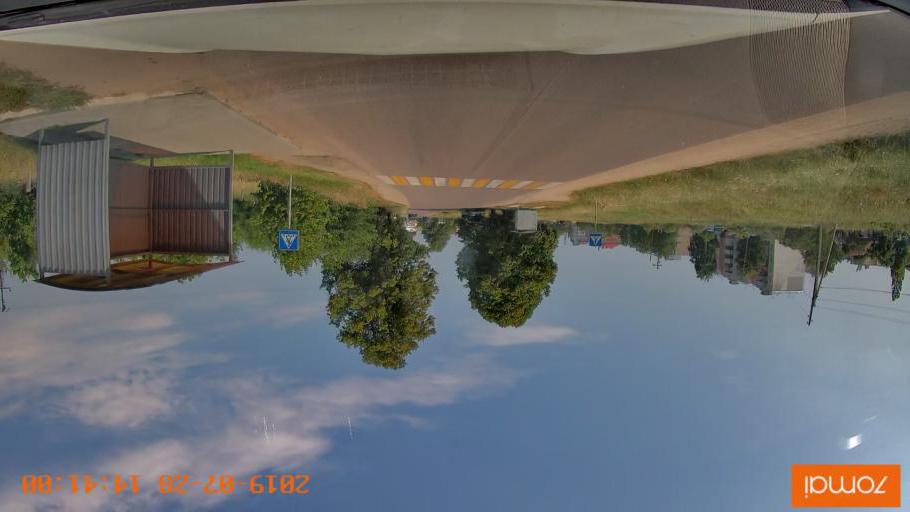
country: RU
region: Kaliningrad
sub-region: Gorod Kaliningrad
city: Yantarnyy
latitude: 54.8544
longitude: 19.9518
